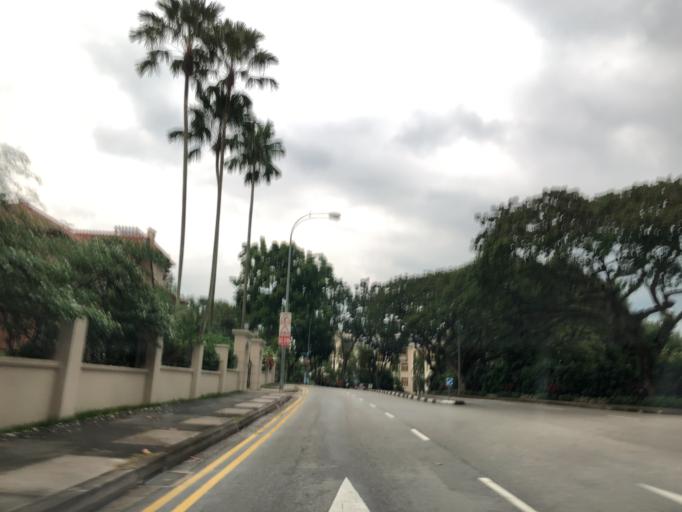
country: SG
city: Singapore
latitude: 1.3108
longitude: 103.8258
